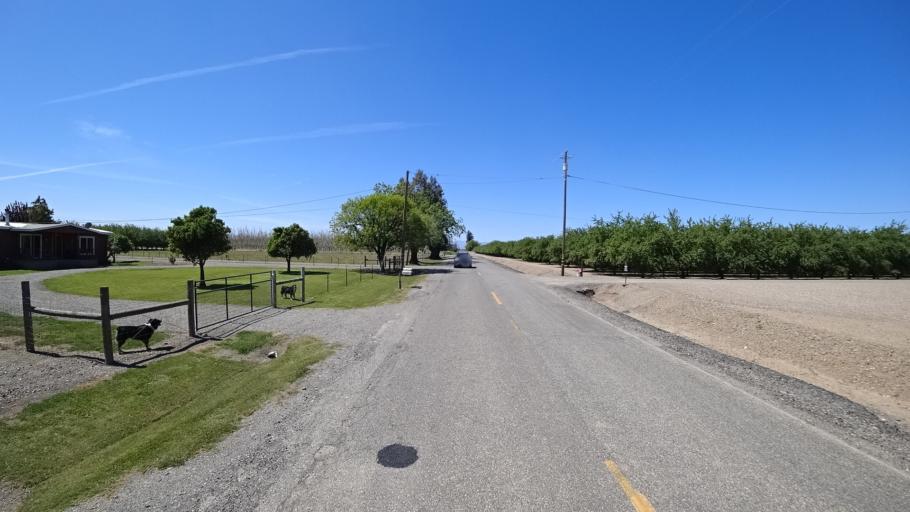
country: US
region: California
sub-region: Glenn County
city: Orland
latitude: 39.7249
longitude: -122.1075
